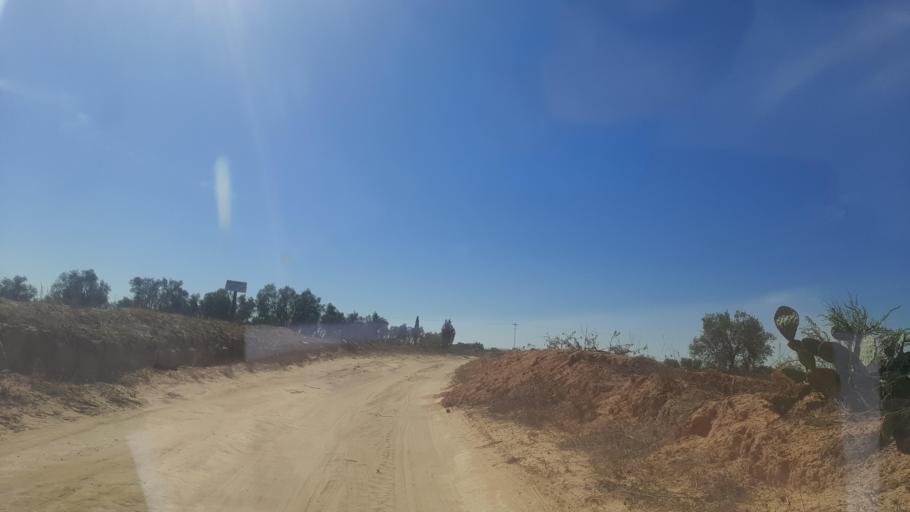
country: TN
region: Safaqis
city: Sfax
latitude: 34.8309
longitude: 10.5564
